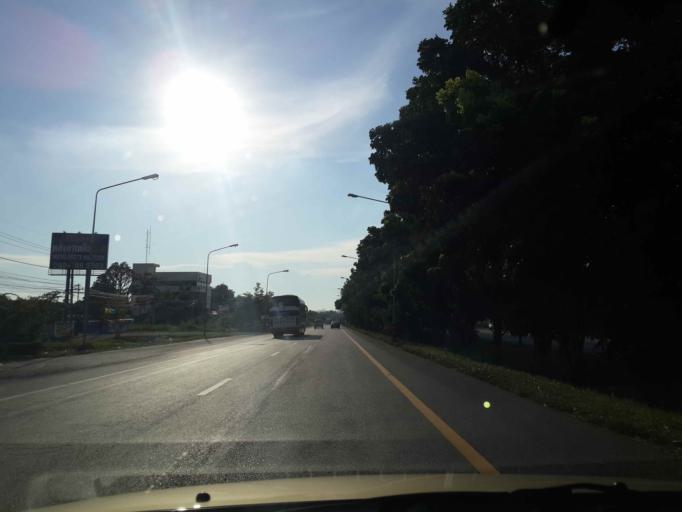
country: TH
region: Chon Buri
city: Bang Lamung
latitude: 12.9880
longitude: 100.9452
